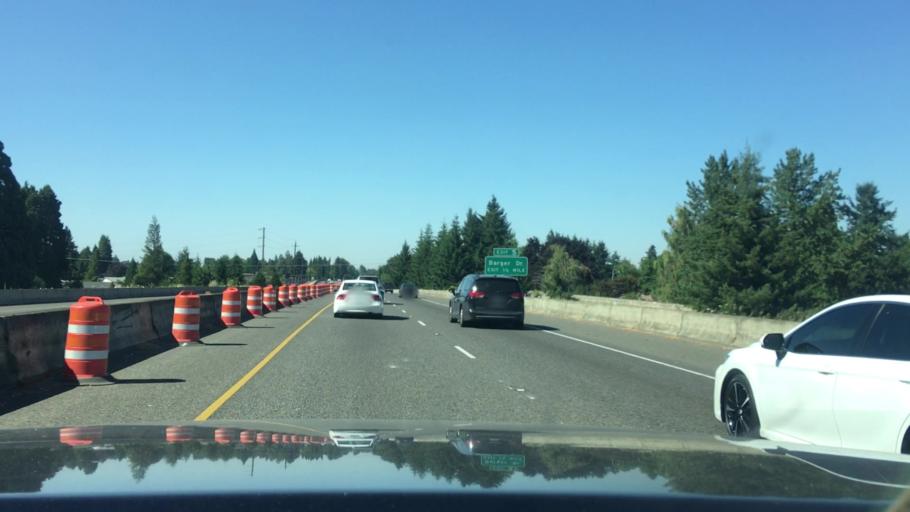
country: US
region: Oregon
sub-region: Lane County
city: Eugene
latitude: 44.0710
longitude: -123.1736
